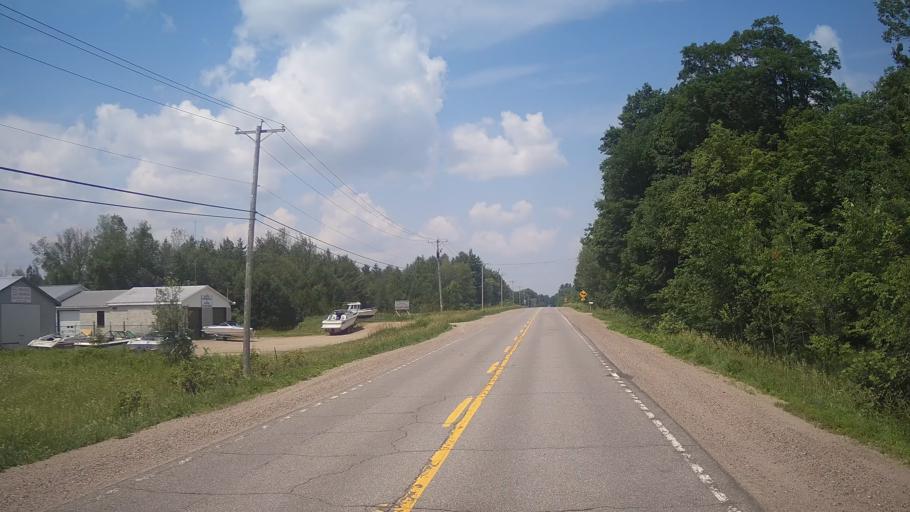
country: CA
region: Quebec
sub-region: Outaouais
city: Shawville
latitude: 45.5707
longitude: -76.4362
